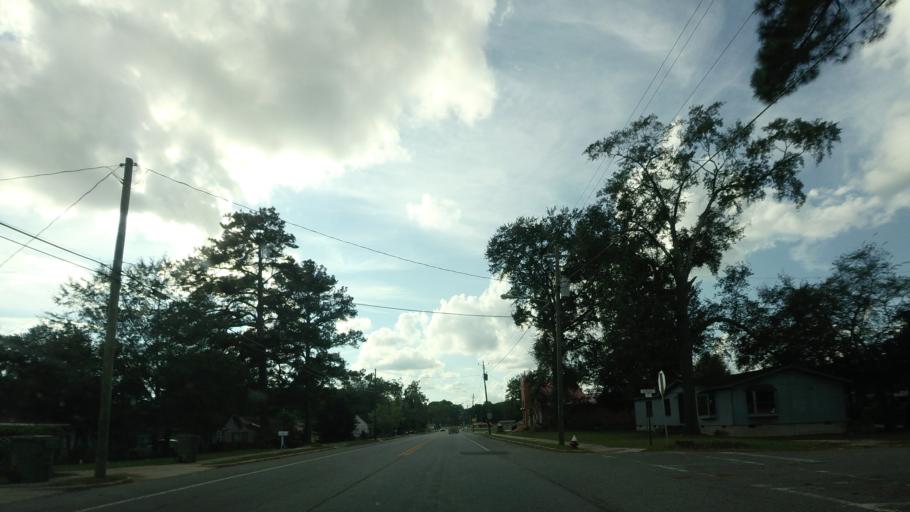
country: US
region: Georgia
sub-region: Pulaski County
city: Hawkinsville
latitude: 32.2847
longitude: -83.4772
